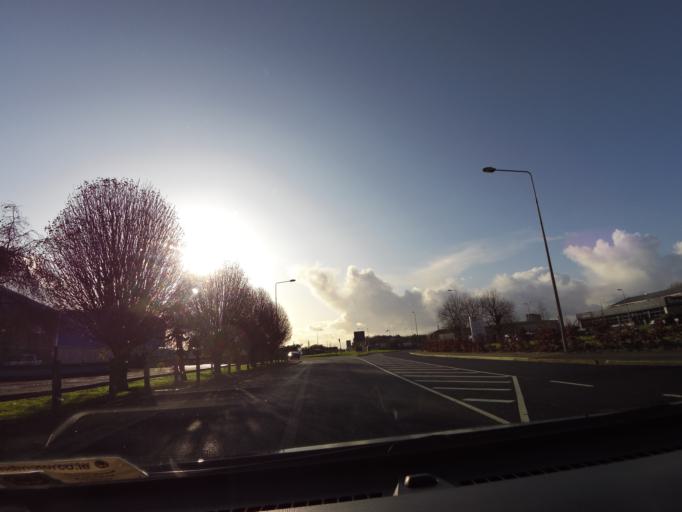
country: IE
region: Munster
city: Moyross
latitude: 52.6528
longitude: -8.6562
